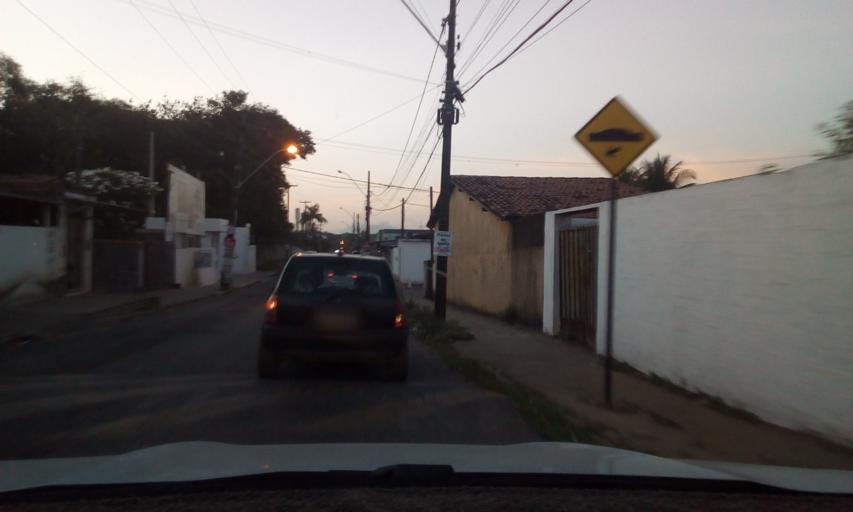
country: BR
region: Paraiba
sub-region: Bayeux
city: Bayeux
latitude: -7.1737
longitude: -34.9120
